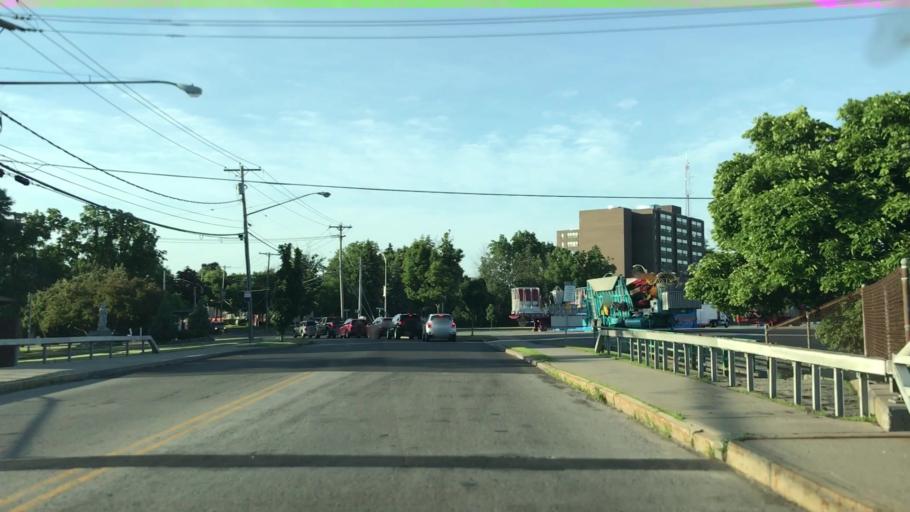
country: US
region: New York
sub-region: Erie County
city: Lancaster
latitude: 42.9012
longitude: -78.6732
